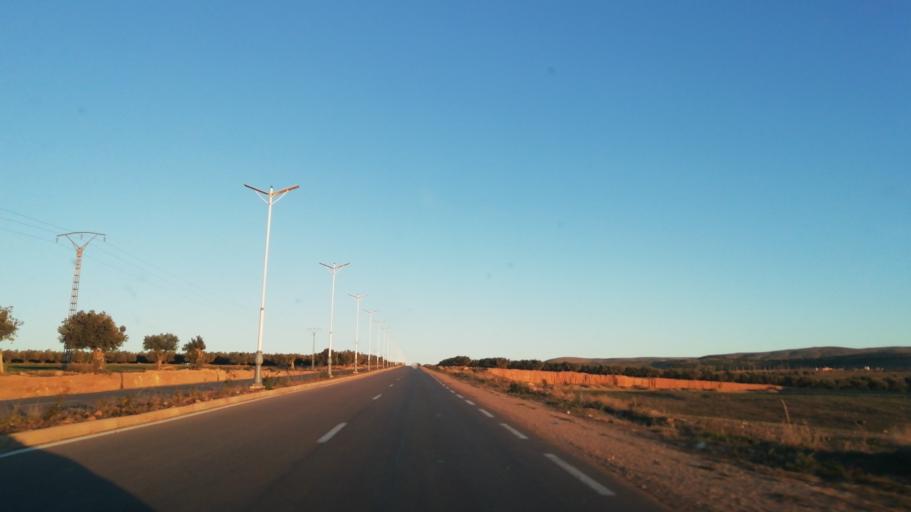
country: DZ
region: Saida
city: Saida
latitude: 34.8653
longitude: 0.1854
